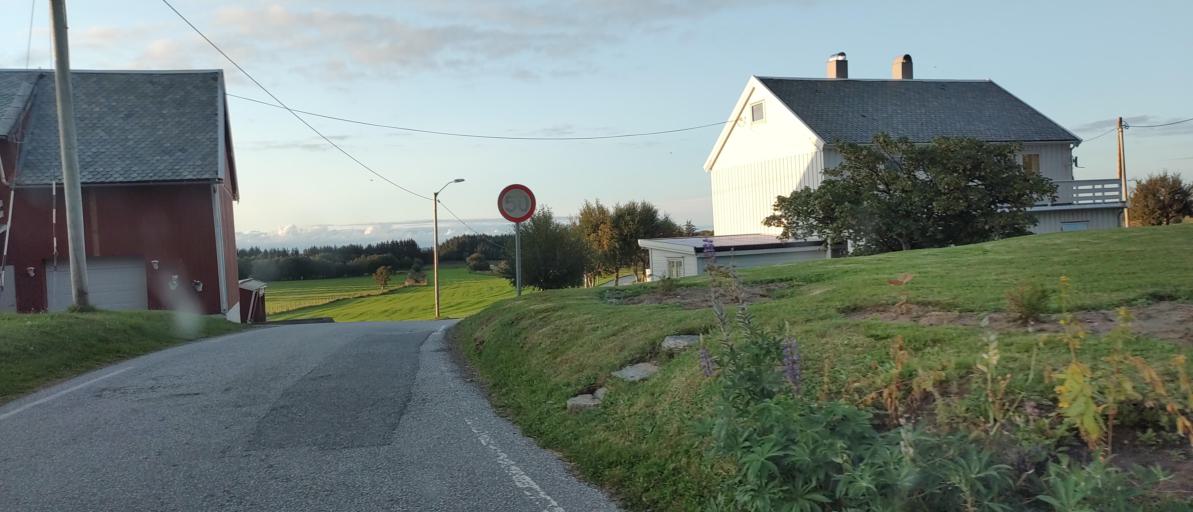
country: NO
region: More og Romsdal
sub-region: Fraena
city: Elnesvagen
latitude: 62.9886
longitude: 7.2107
